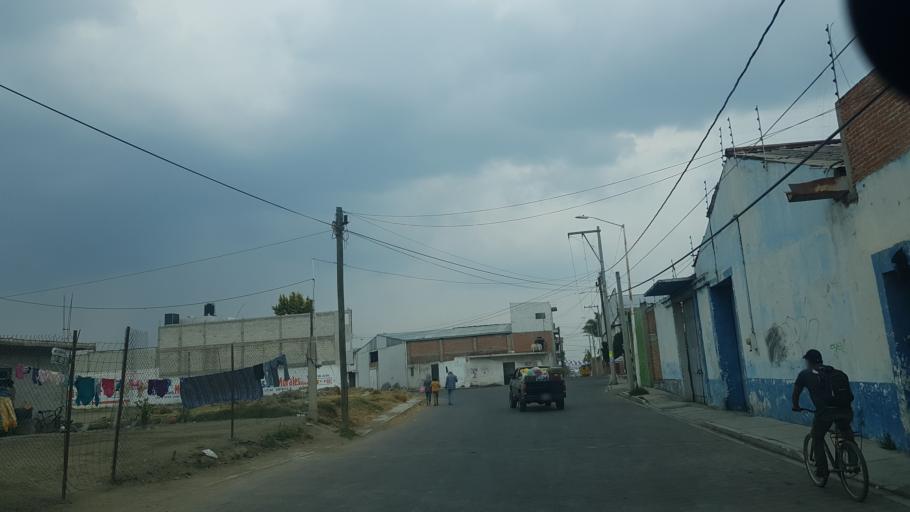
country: MX
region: Puebla
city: Huejotzingo
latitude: 19.1649
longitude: -98.4099
